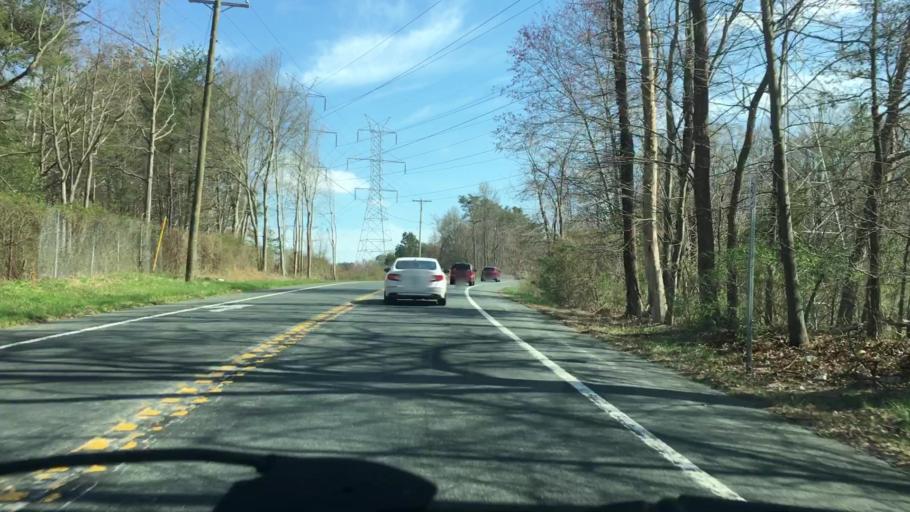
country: US
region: Maryland
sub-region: Anne Arundel County
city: Maryland City
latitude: 39.0402
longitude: -76.7953
